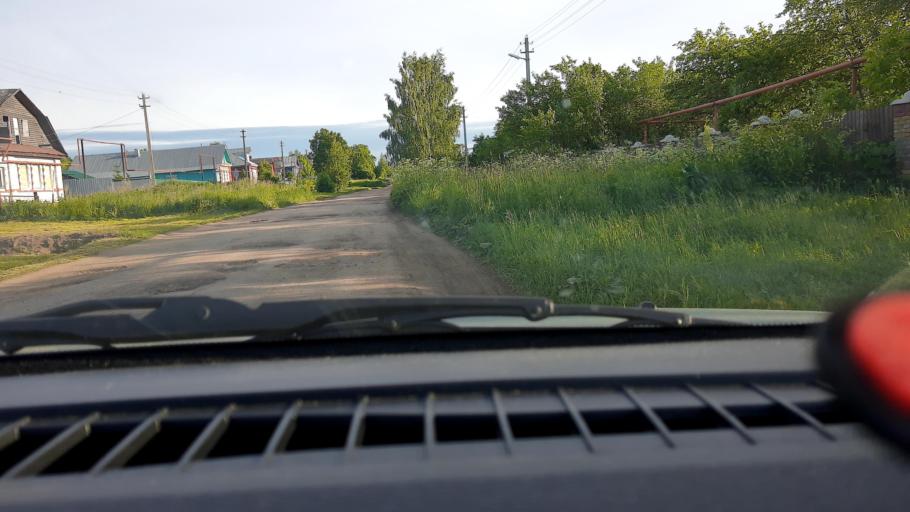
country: RU
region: Nizjnij Novgorod
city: Afonino
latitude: 56.1301
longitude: 44.0299
